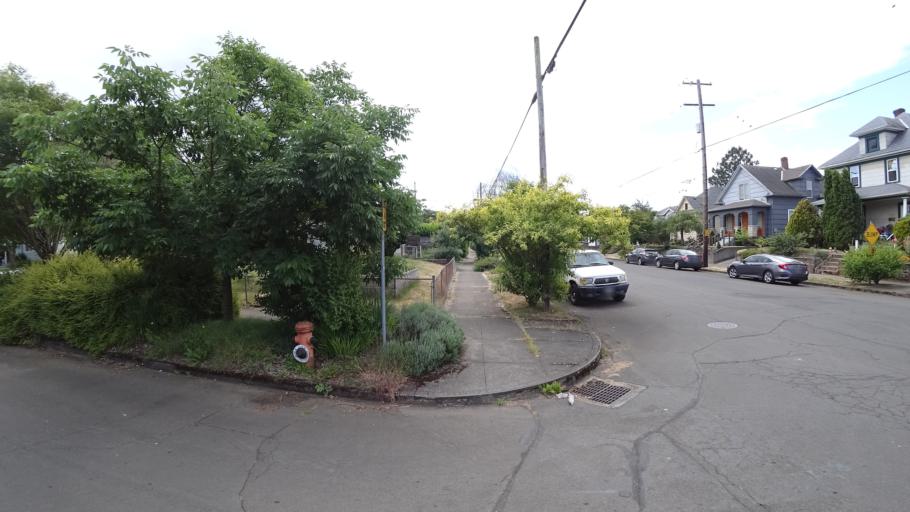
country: US
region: Oregon
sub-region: Washington County
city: West Haven
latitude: 45.5816
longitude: -122.7365
